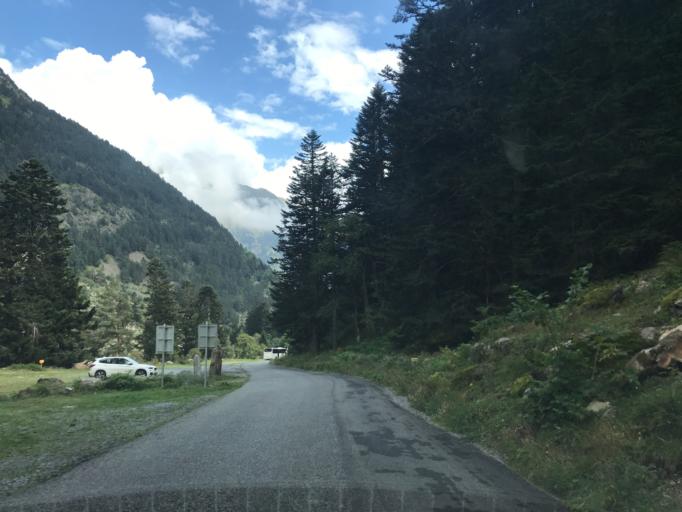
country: FR
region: Midi-Pyrenees
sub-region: Departement des Hautes-Pyrenees
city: Saint-Lary-Soulan
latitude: 42.8195
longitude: 0.1868
